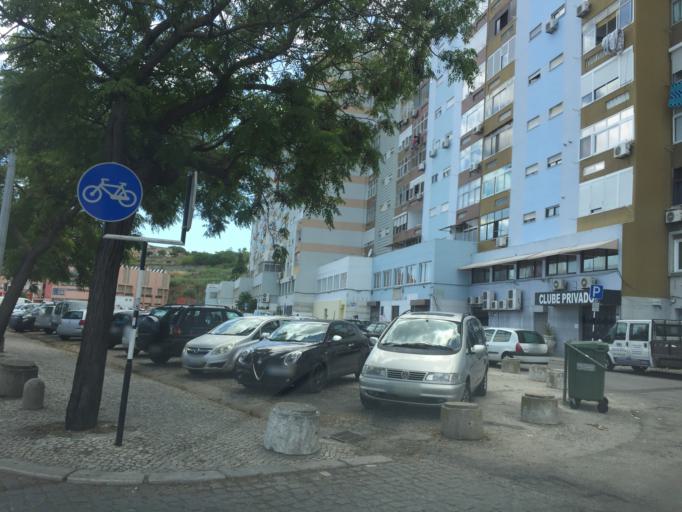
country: PT
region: Setubal
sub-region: Almada
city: Cacilhas
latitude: 38.6839
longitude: -9.1474
